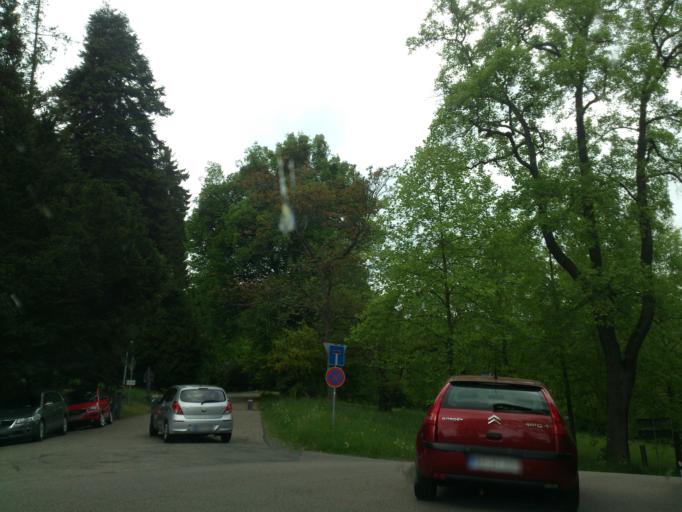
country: DE
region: Hesse
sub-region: Regierungsbezirk Kassel
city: Baunatal
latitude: 51.3171
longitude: 9.4135
